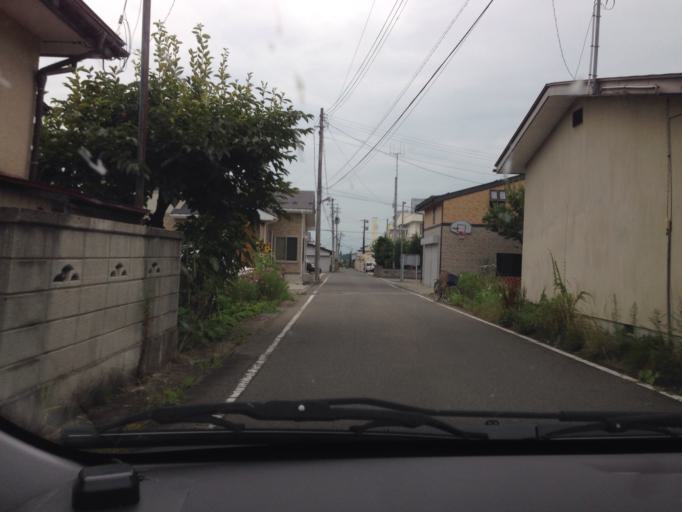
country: JP
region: Fukushima
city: Kitakata
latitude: 37.4666
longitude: 139.8473
